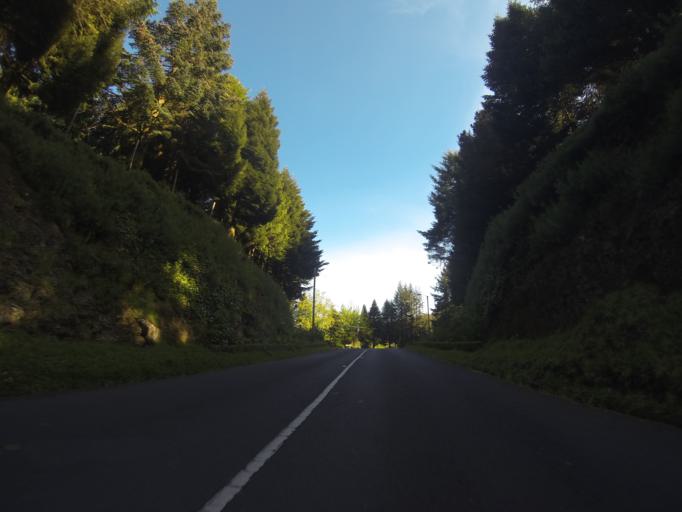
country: PT
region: Madeira
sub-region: Funchal
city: Nossa Senhora do Monte
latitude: 32.7103
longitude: -16.8879
